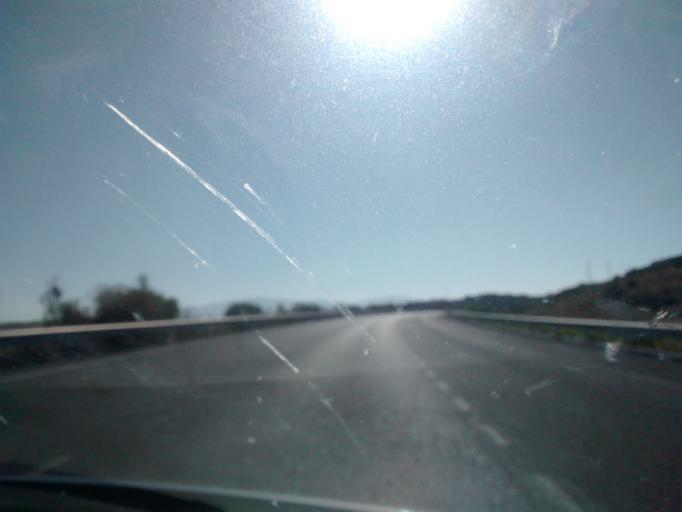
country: ES
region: Andalusia
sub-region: Provincia de Cadiz
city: Alcala de los Gazules
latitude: 36.4724
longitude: -5.8017
